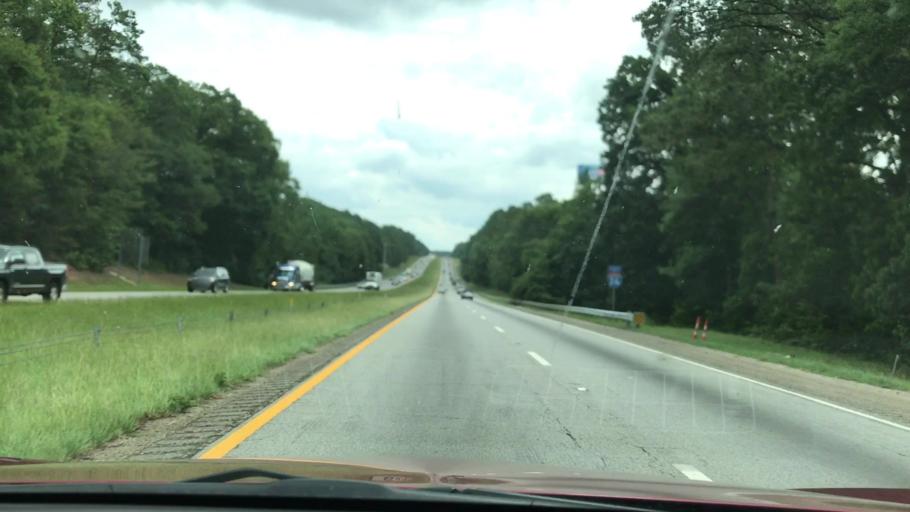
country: US
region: South Carolina
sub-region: Richland County
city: Lake Murray of Richland
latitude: 34.1432
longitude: -81.2321
